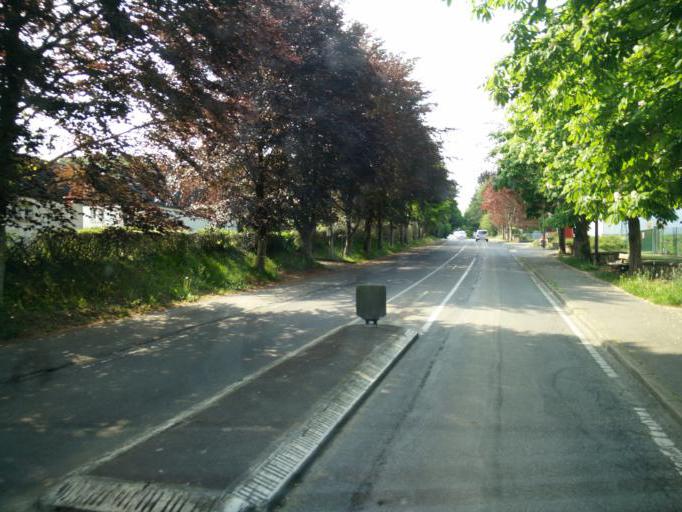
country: FR
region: Brittany
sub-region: Departement du Finistere
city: Moelan-sur-Mer
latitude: 47.8081
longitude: -3.6277
